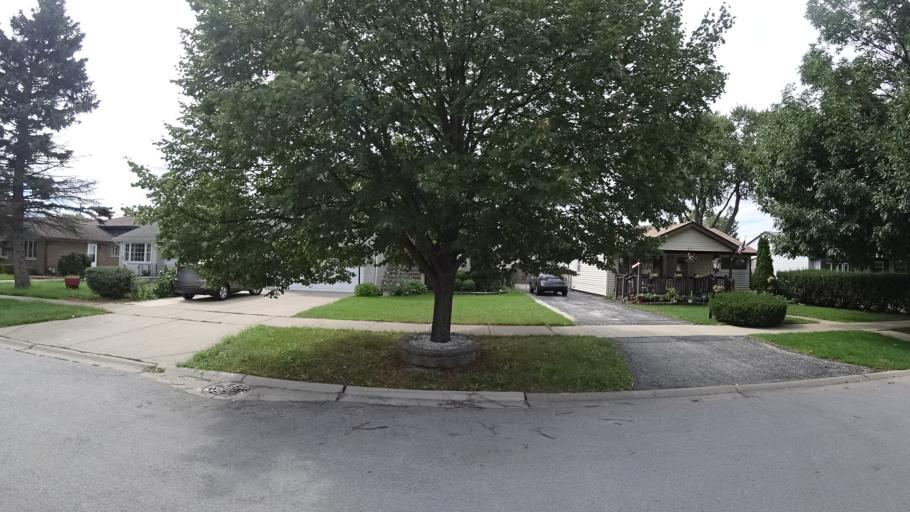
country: US
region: Illinois
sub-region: Cook County
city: Chicago Ridge
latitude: 41.7164
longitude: -87.7883
